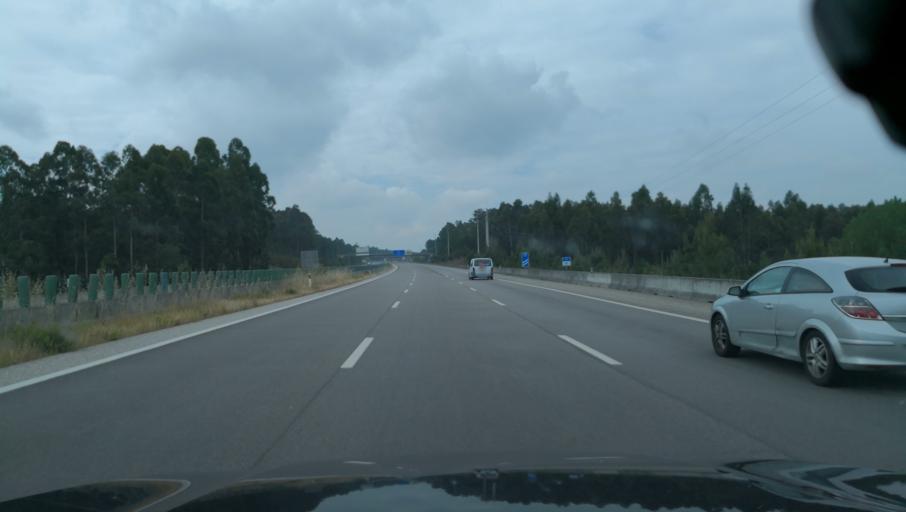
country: PT
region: Leiria
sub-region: Leiria
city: Monte Redondo
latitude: 39.9045
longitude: -8.8038
